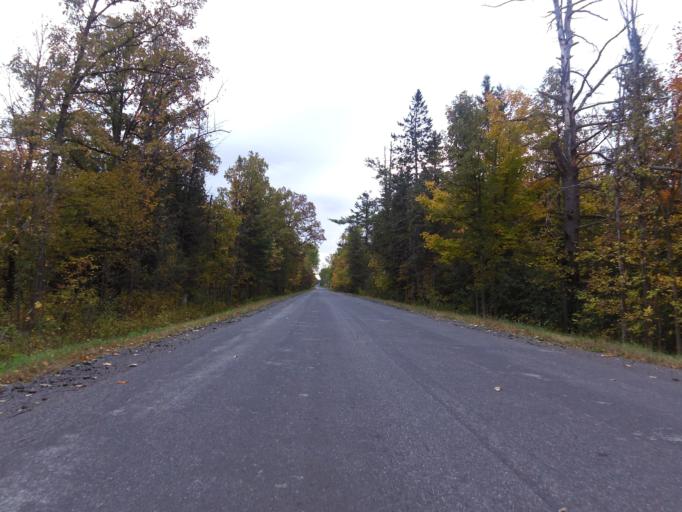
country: CA
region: Ontario
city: Arnprior
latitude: 45.4510
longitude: -76.1323
